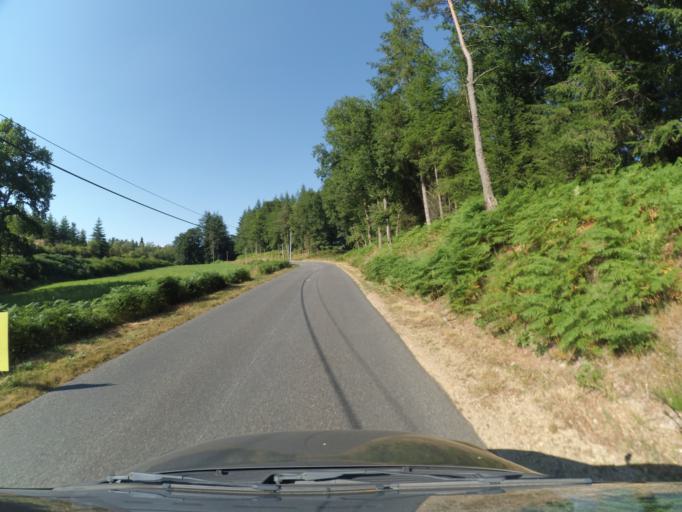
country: FR
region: Limousin
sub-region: Departement de la Haute-Vienne
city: Peyrat-le-Chateau
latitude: 45.7692
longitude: 1.8265
